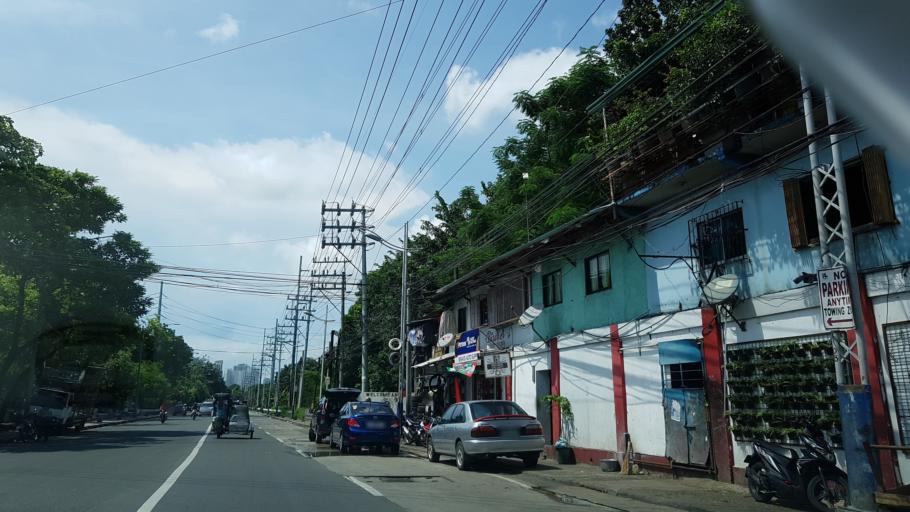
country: PH
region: Metro Manila
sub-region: Makati City
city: Makati City
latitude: 14.5291
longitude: 121.0264
